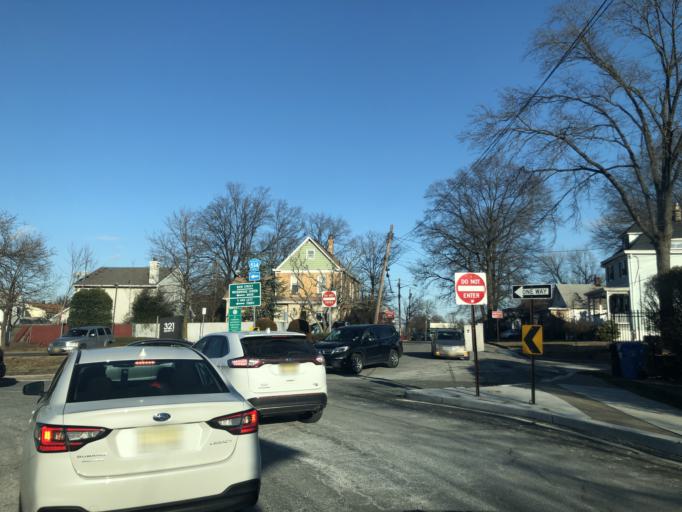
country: US
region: New Jersey
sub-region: Middlesex County
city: Woodbridge
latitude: 40.5494
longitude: -74.2904
